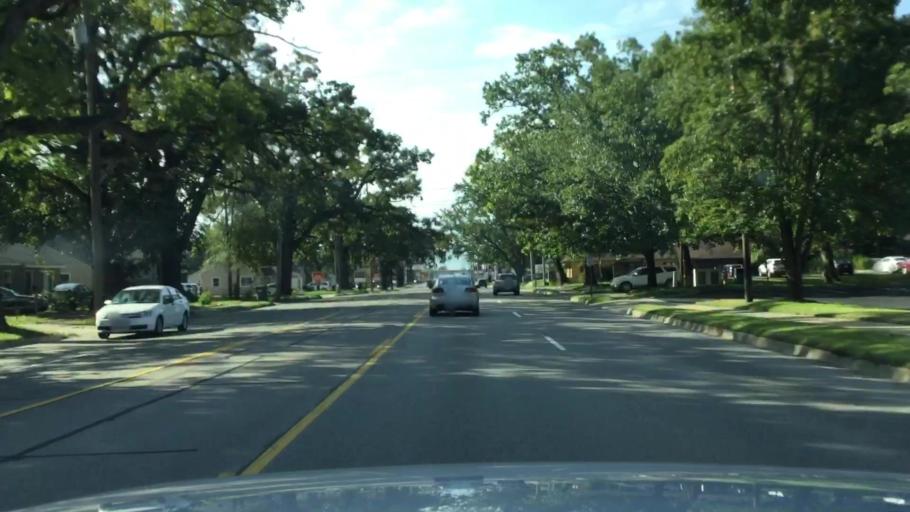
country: US
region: Michigan
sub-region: Kalamazoo County
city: Kalamazoo
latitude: 42.2501
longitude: -85.5896
